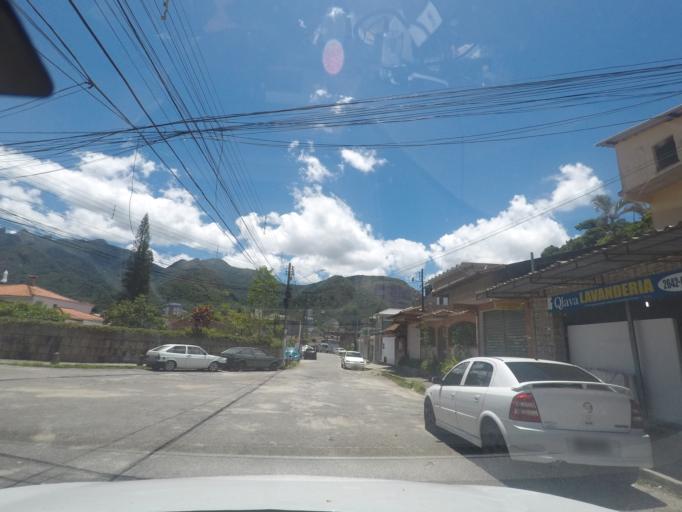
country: BR
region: Rio de Janeiro
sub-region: Teresopolis
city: Teresopolis
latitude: -22.4330
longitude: -42.9728
